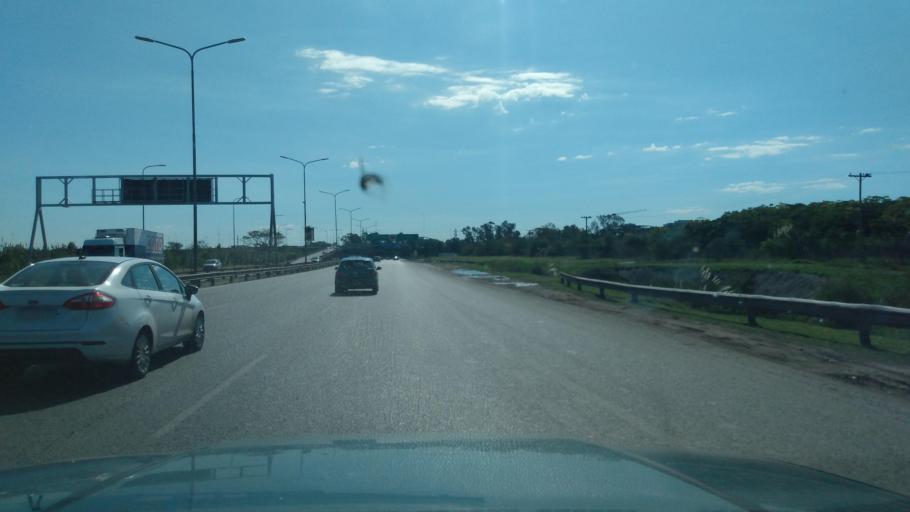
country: AR
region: Buenos Aires
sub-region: Partido de Tigre
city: Tigre
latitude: -34.4927
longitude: -58.5955
